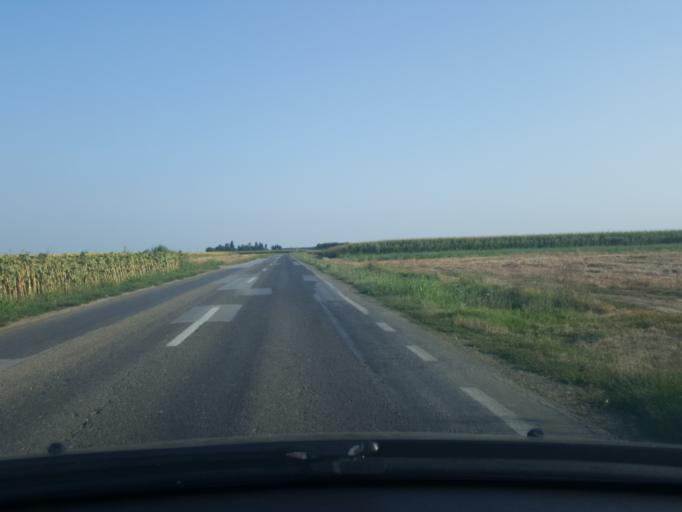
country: RS
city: Hrtkovci
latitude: 44.8655
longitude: 19.7712
